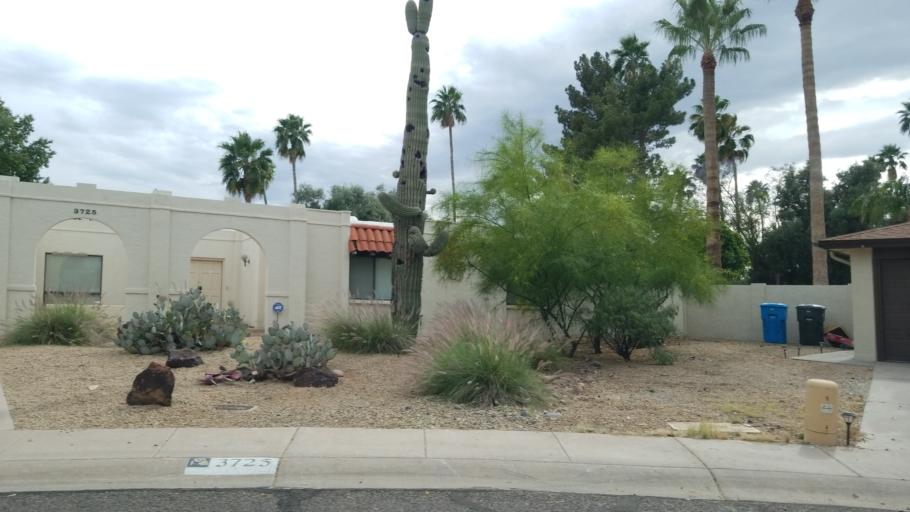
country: US
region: Arizona
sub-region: Maricopa County
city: Paradise Valley
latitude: 33.5891
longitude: -112.0014
